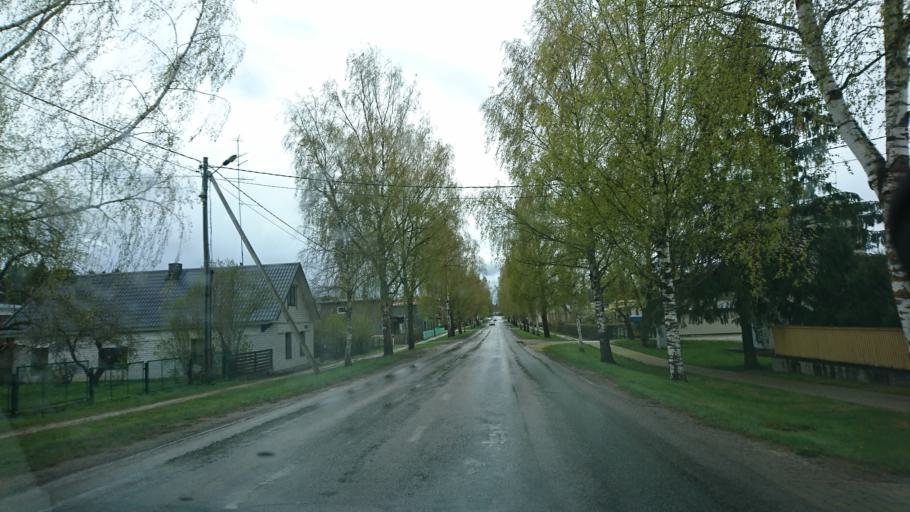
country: EE
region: Laeaene-Virumaa
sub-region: Rakvere linn
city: Rakvere
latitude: 59.3311
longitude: 26.3634
